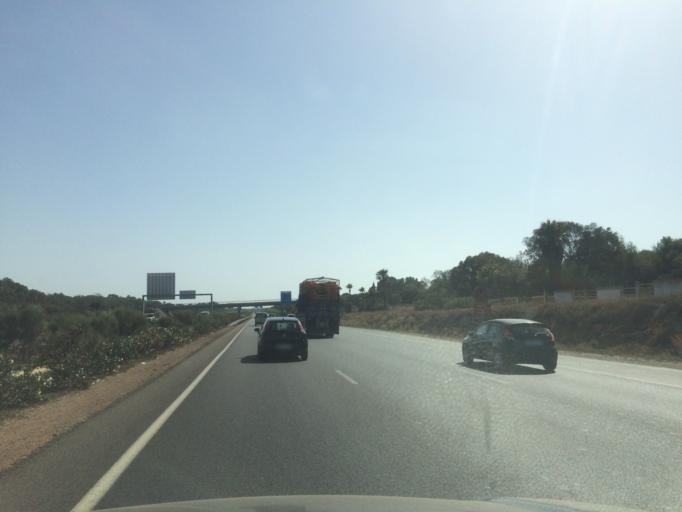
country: MA
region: Rabat-Sale-Zemmour-Zaer
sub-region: Skhirate-Temara
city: Temara
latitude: 33.9444
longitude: -6.9236
